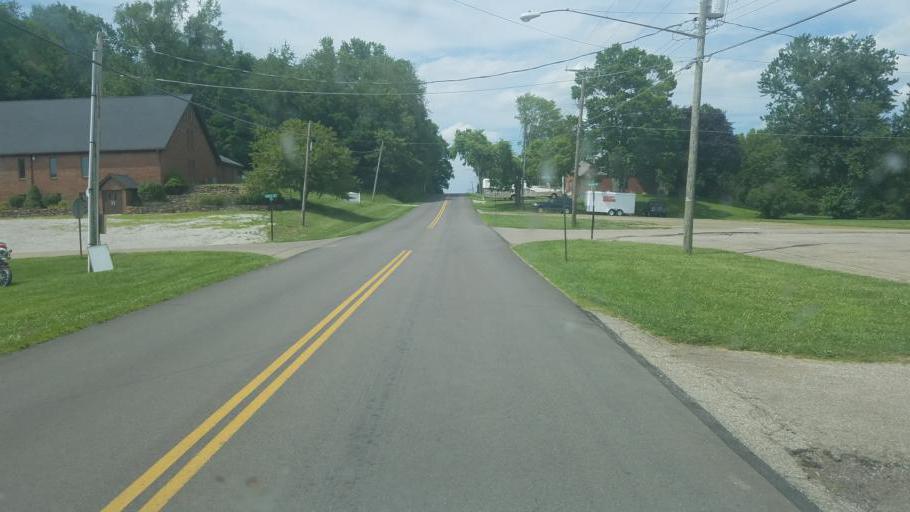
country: US
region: Ohio
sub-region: Knox County
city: Fredericktown
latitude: 40.4720
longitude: -82.5411
